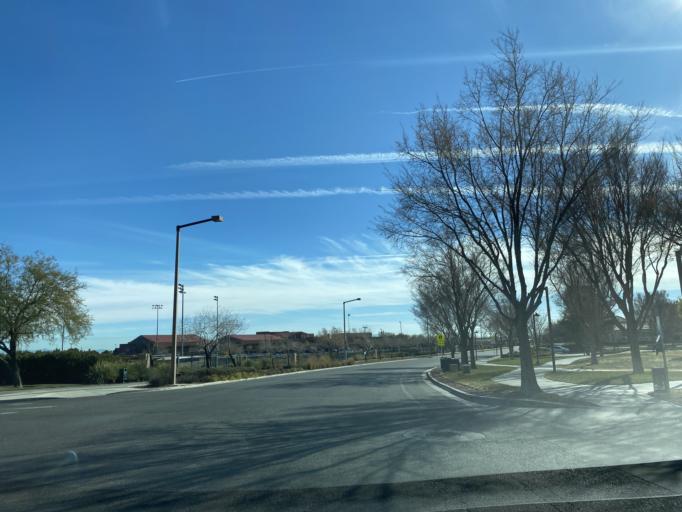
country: US
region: Nevada
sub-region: Clark County
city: Summerlin South
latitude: 36.1563
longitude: -115.3200
